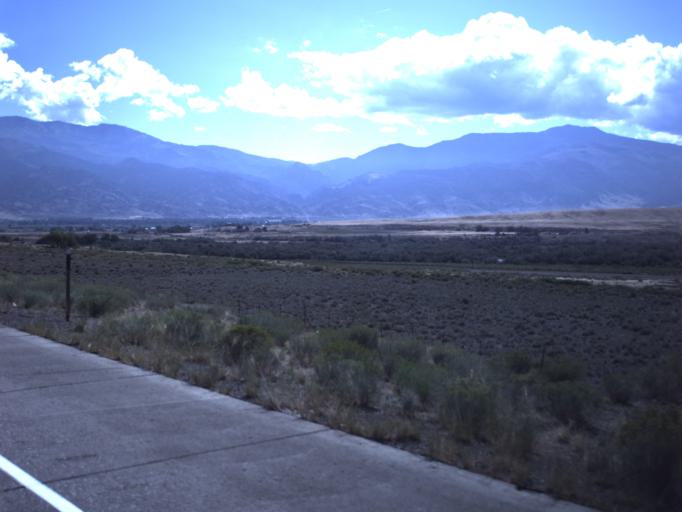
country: US
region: Utah
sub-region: Sevier County
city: Monroe
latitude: 38.6583
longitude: -112.1930
